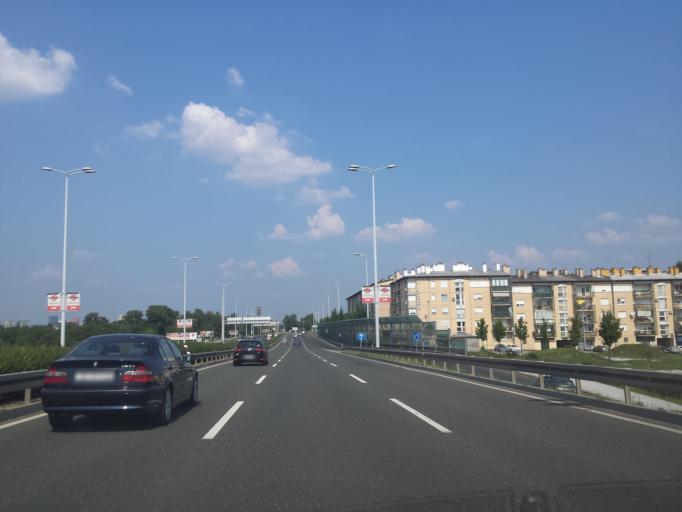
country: HR
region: Grad Zagreb
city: Novi Zagreb
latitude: 45.7741
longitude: 15.9436
